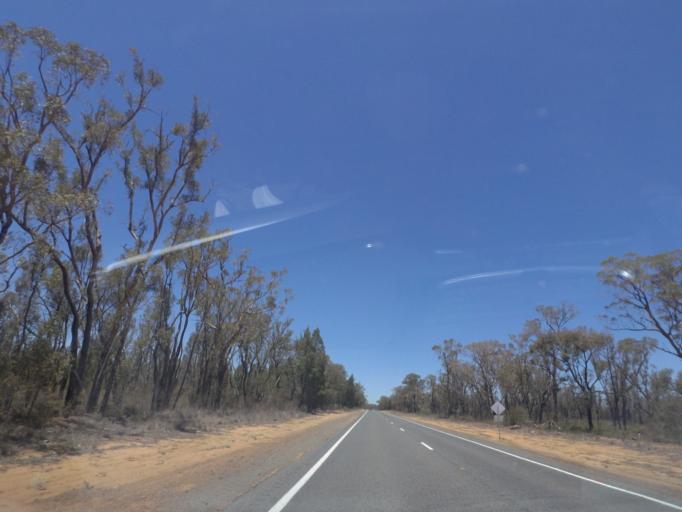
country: AU
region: New South Wales
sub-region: Narrabri
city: Narrabri
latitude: -30.7128
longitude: 149.5292
